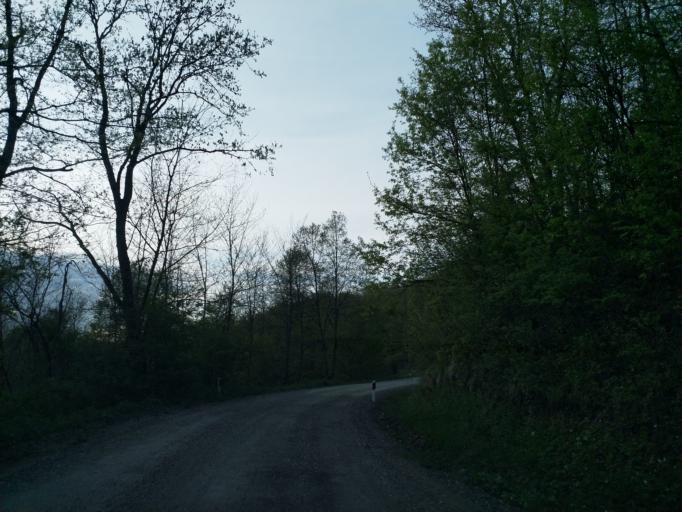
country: RS
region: Central Serbia
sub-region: Pomoravski Okrug
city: Despotovac
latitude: 43.9568
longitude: 21.5674
